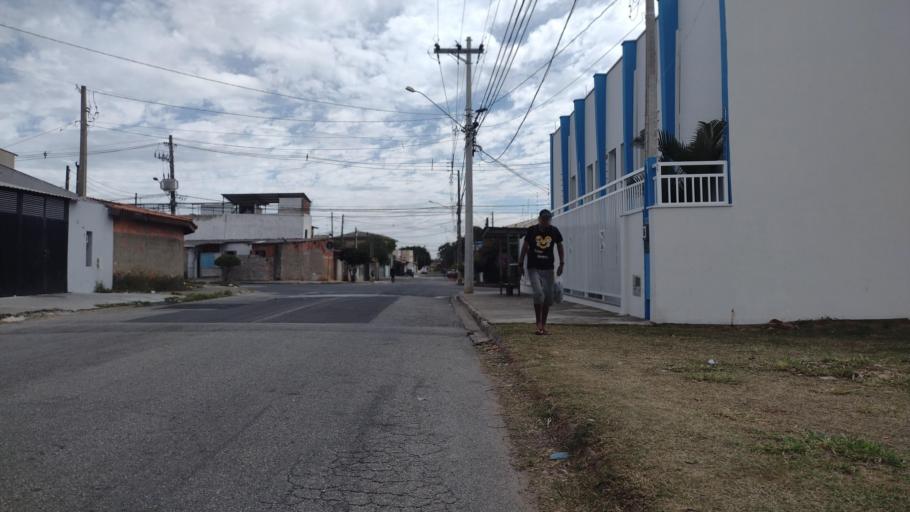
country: BR
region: Sao Paulo
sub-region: Sorocaba
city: Sorocaba
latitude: -23.4256
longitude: -47.4535
